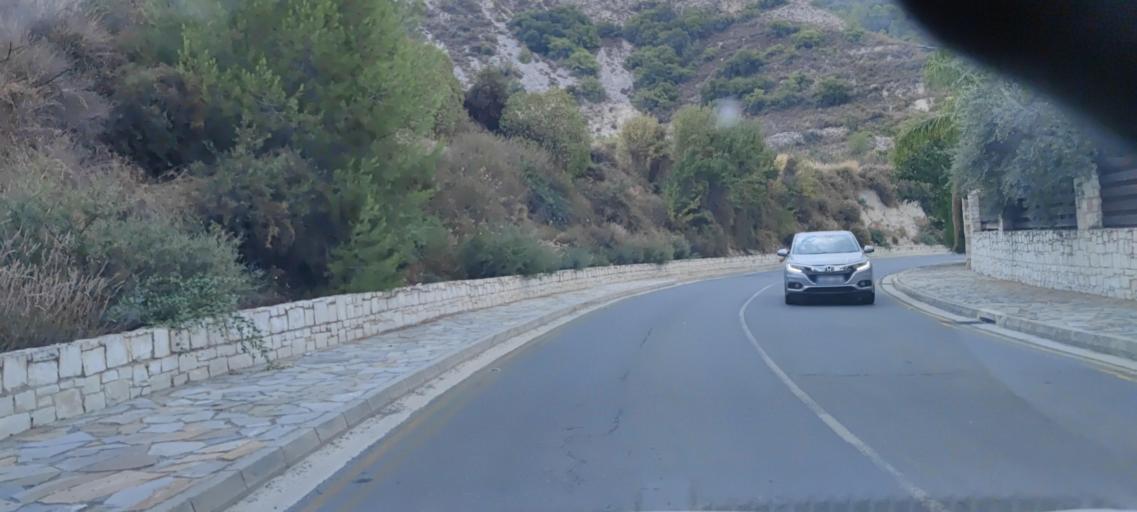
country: CY
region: Limassol
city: Pelendri
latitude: 34.8426
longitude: 32.9151
